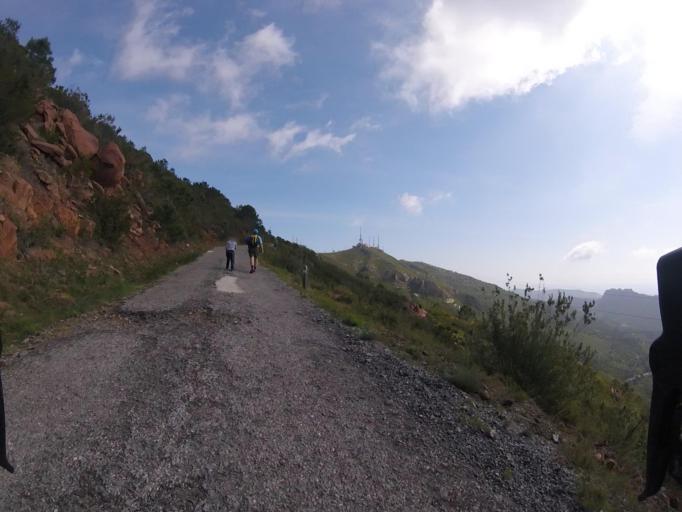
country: ES
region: Valencia
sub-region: Provincia de Castello
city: Benicassim
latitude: 40.0792
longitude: 0.0232
